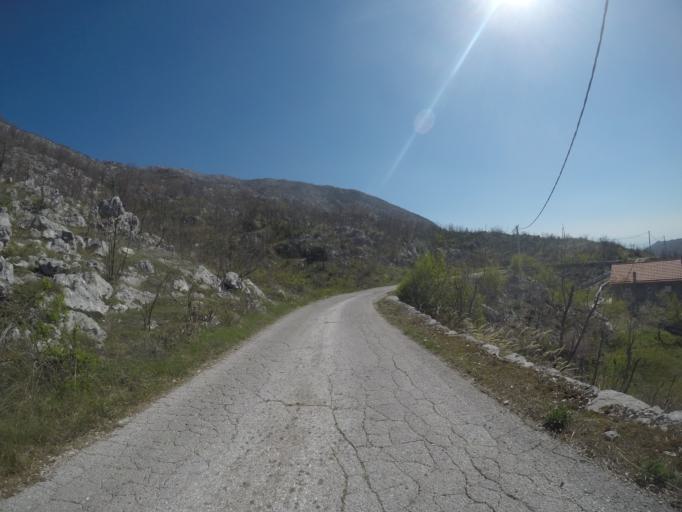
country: ME
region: Danilovgrad
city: Danilovgrad
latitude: 42.5315
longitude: 19.0232
